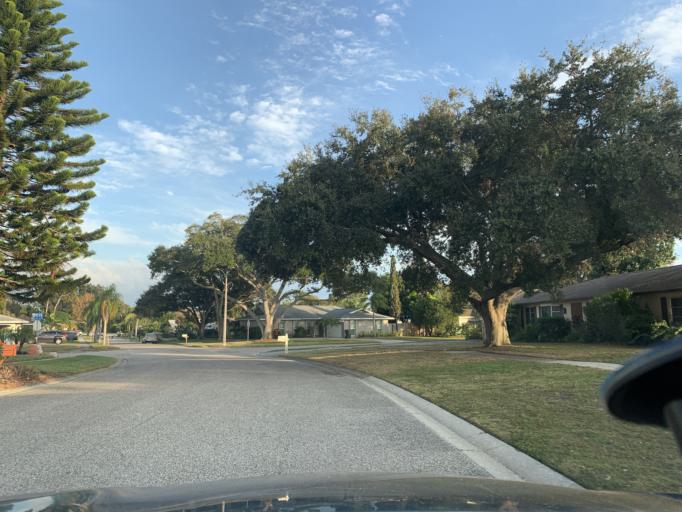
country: US
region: Florida
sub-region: Pinellas County
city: Ridgecrest
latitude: 27.8908
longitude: -82.7940
